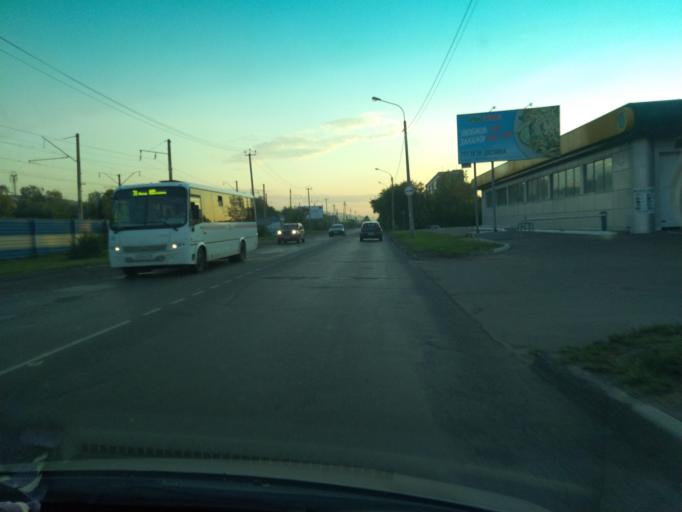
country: RU
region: Krasnoyarskiy
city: Krasnoyarsk
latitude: 55.9836
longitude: 92.8760
